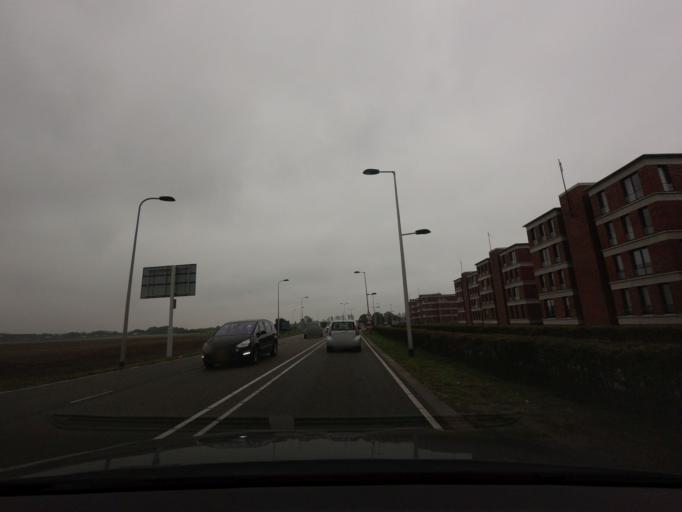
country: NL
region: South Holland
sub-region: Gemeente Noordwijk
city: Noordwijk-Binnen
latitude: 52.2368
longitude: 4.4579
